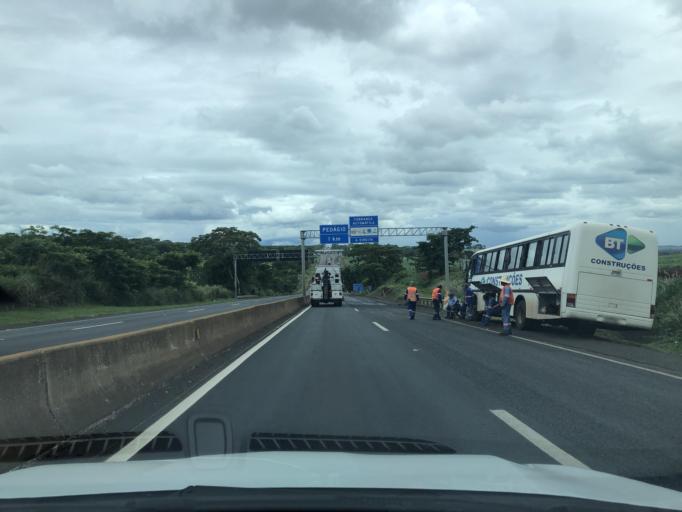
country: BR
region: Sao Paulo
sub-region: Igarapava
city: Igarapava
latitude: -19.9067
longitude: -47.8354
